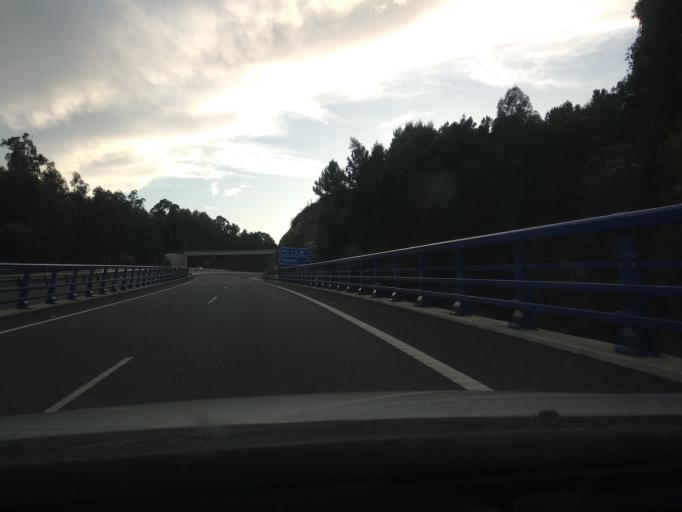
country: ES
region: Galicia
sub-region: Provincia de Pontevedra
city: Moana
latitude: 42.2990
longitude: -8.6804
